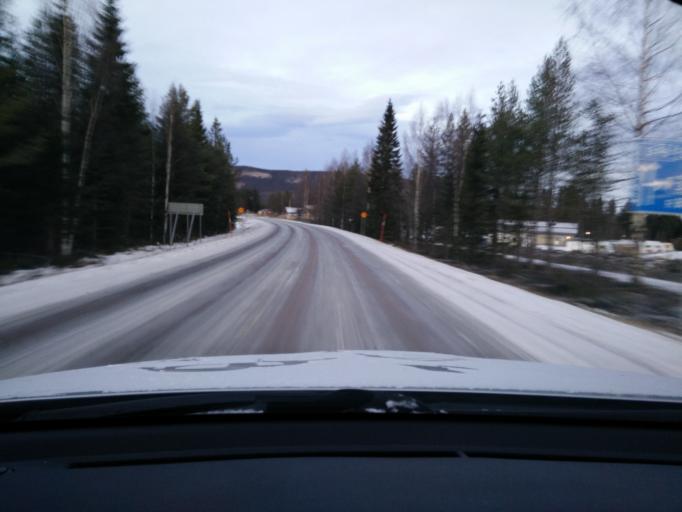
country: SE
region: Jaemtland
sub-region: Bergs Kommun
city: Hoverberg
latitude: 62.4770
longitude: 14.2283
